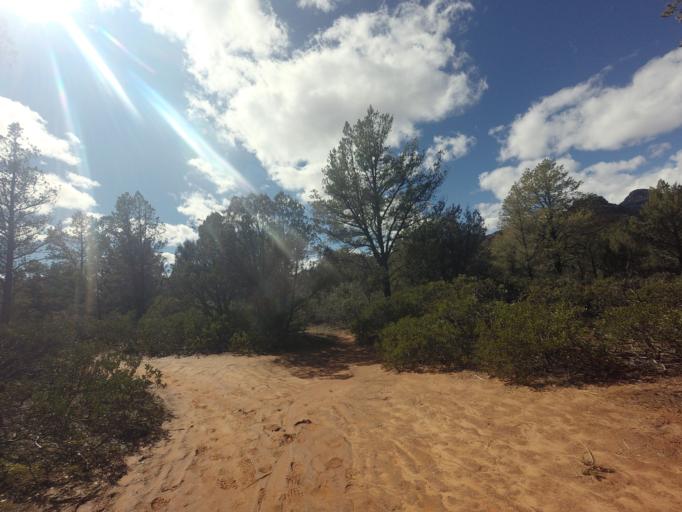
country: US
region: Arizona
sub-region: Yavapai County
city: West Sedona
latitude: 34.9006
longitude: -111.8251
